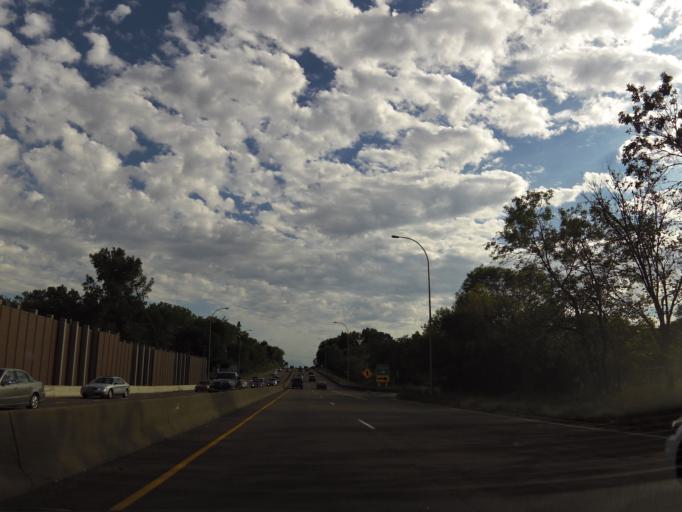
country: US
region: Minnesota
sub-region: Hennepin County
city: Minnetonka Mills
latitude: 44.9687
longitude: -93.4007
